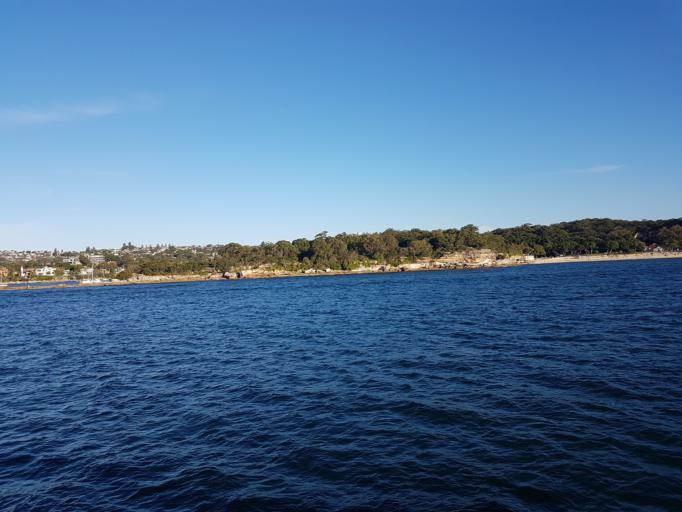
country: AU
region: New South Wales
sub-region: Woollahra
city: Point Piper
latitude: -33.8458
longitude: 151.2672
